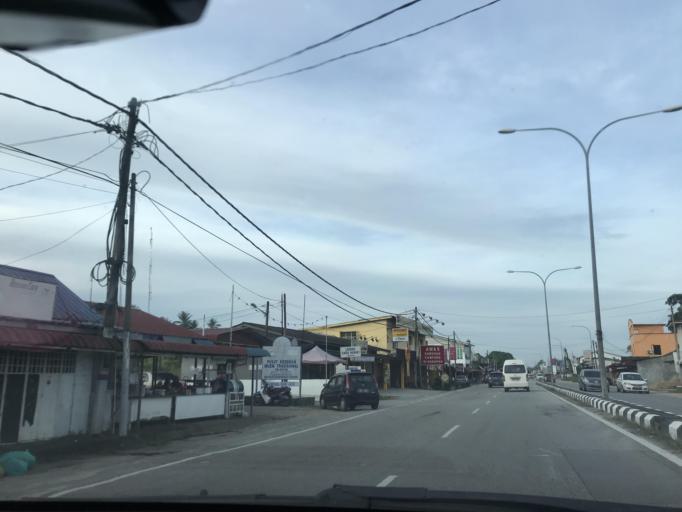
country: MY
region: Kelantan
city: Kota Bharu
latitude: 6.1131
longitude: 102.2139
